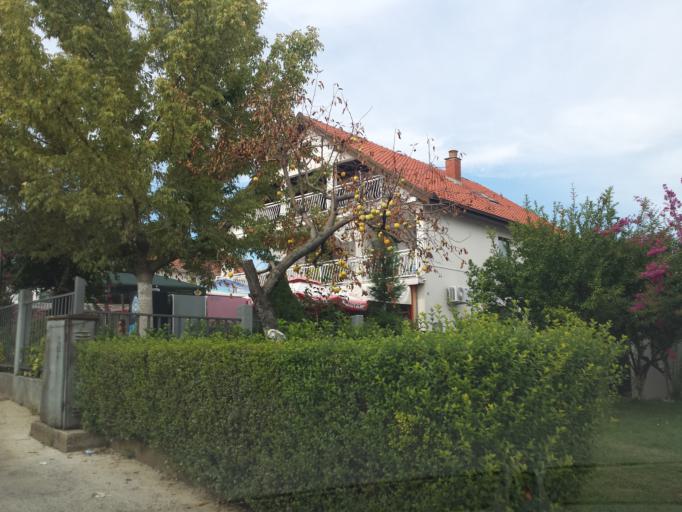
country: BA
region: Federation of Bosnia and Herzegovina
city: Citluk
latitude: 43.2003
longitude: 17.6717
